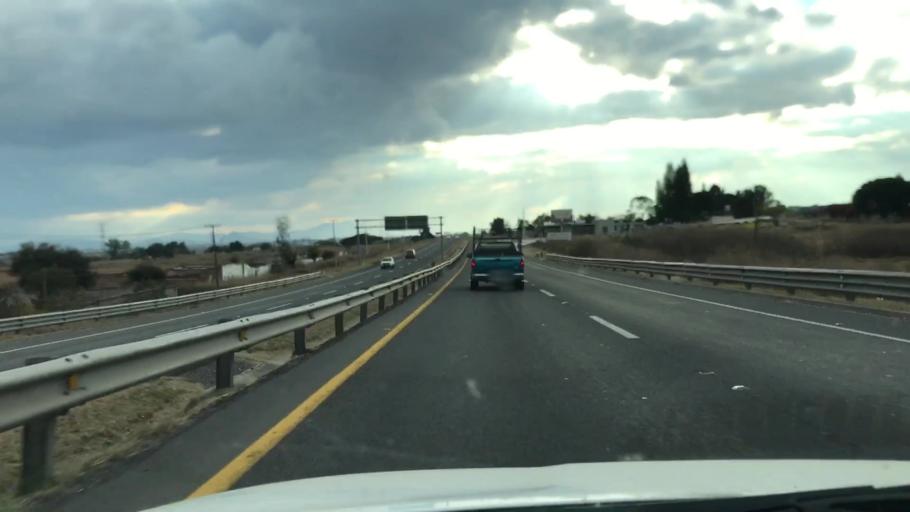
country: MX
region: Guanajuato
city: Penjamo
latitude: 20.4138
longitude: -101.7319
